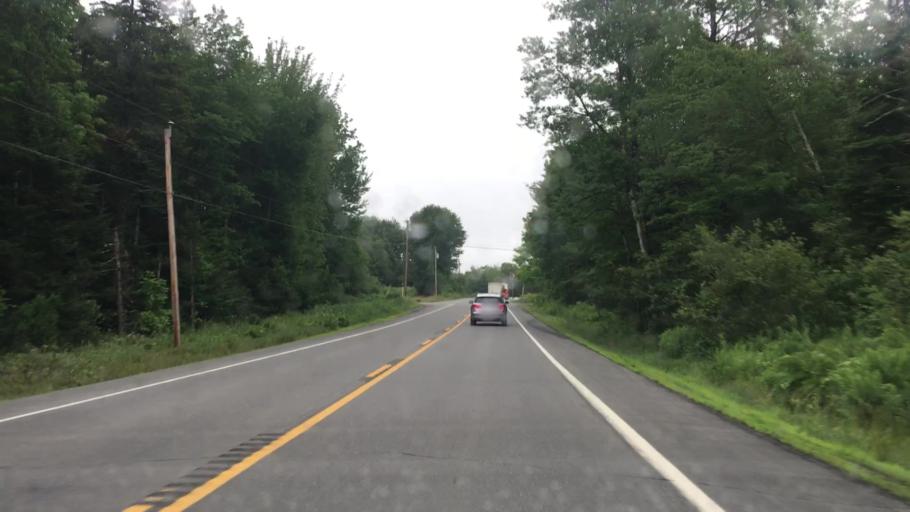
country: US
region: Maine
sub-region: Knox County
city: Washington
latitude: 44.2513
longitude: -69.4121
